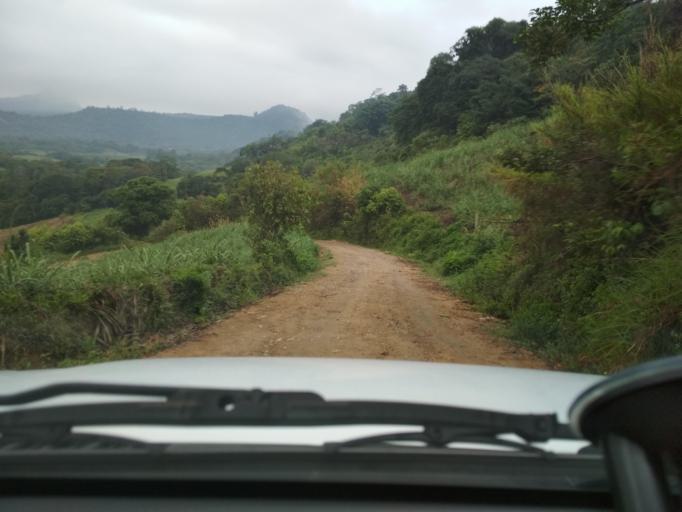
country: MX
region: Veracruz
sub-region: Fortin
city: Monte Salas
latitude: 18.9234
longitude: -97.0393
